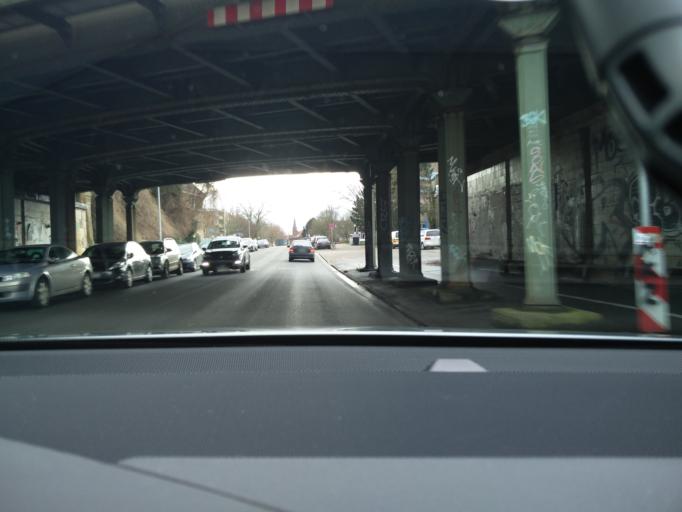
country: DE
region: Lower Saxony
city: Hannover
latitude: 52.3524
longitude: 9.7268
